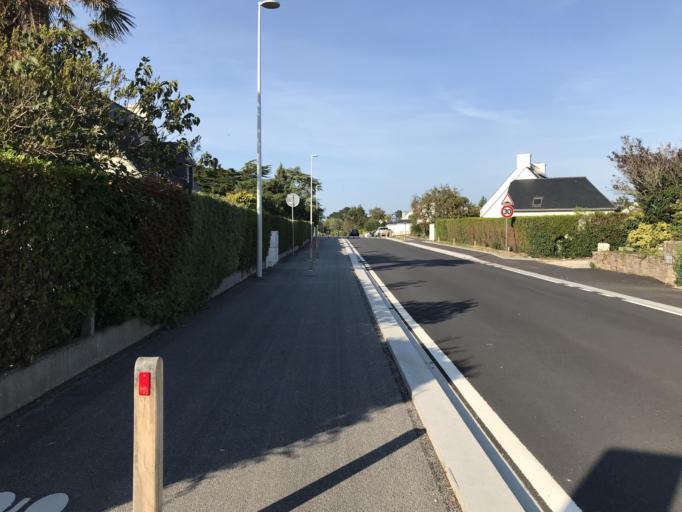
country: FR
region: Brittany
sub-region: Departement du Morbihan
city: Arzon
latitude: 47.5494
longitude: -2.9001
